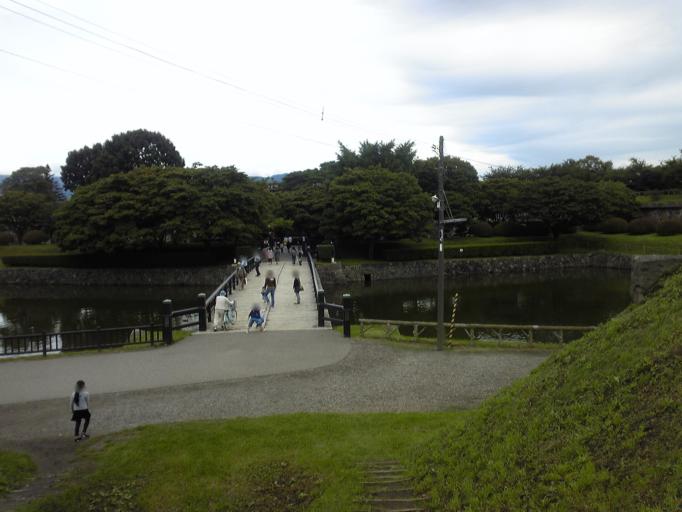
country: JP
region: Hokkaido
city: Hakodate
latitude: 41.7955
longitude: 140.7544
